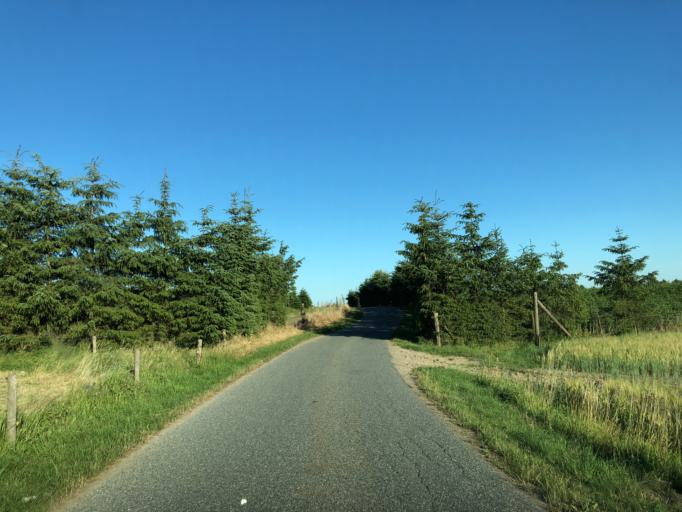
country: DK
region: Central Jutland
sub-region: Skanderborg Kommune
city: Ry
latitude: 55.9765
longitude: 9.8026
